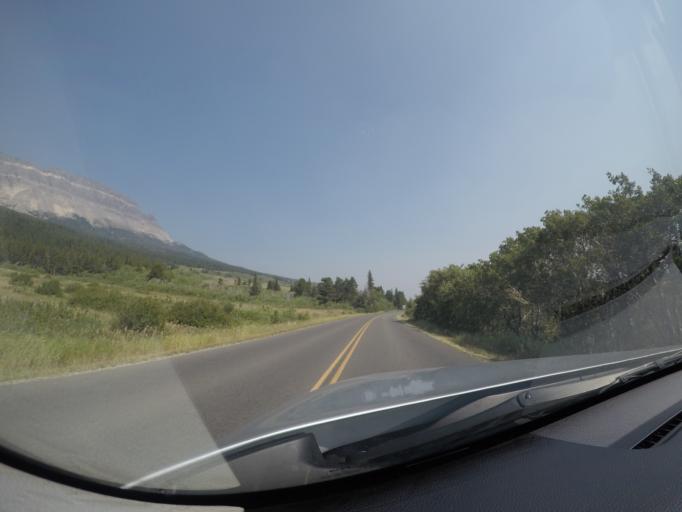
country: US
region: Montana
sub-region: Glacier County
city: North Browning
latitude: 48.7194
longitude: -113.4742
